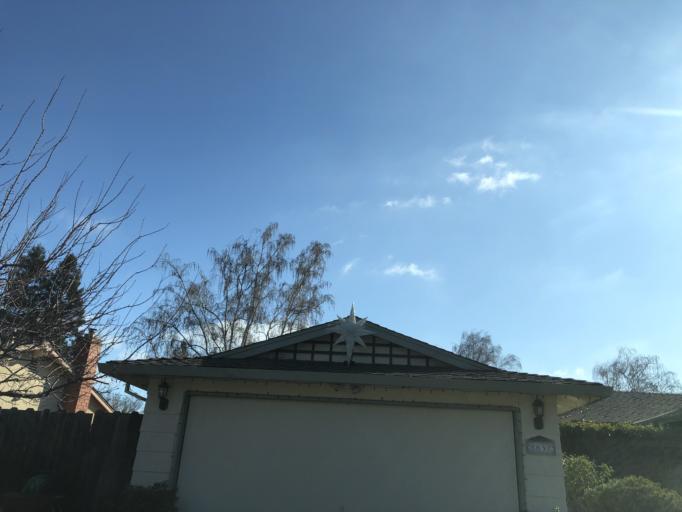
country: US
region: California
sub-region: Sacramento County
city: Rosemont
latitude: 38.5607
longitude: -121.3845
